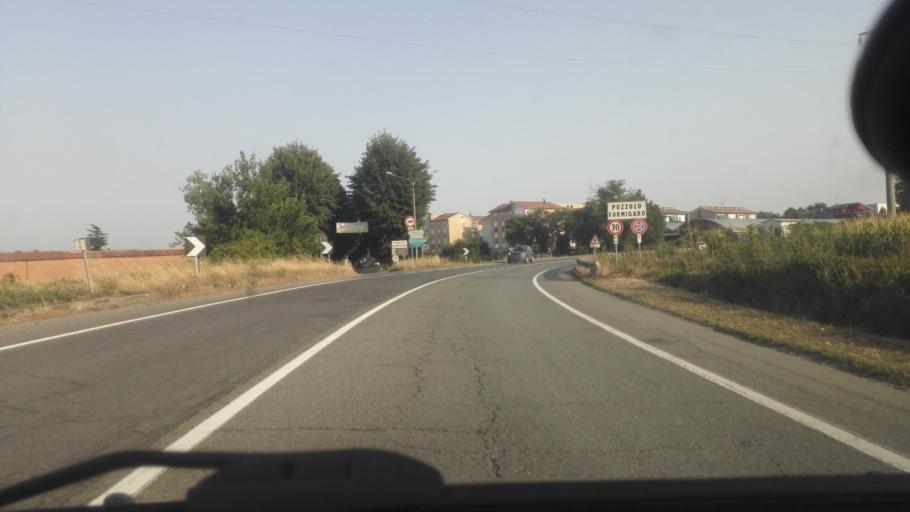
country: IT
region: Piedmont
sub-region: Provincia di Alessandria
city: Pozzolo Formigaro
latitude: 44.7991
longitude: 8.7781
